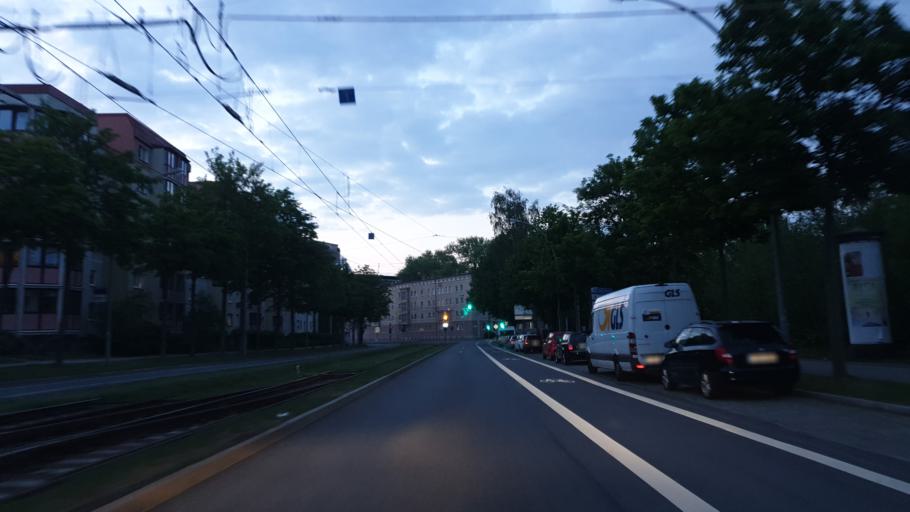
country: DE
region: Saxony
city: Chemnitz
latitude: 50.8269
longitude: 12.9203
